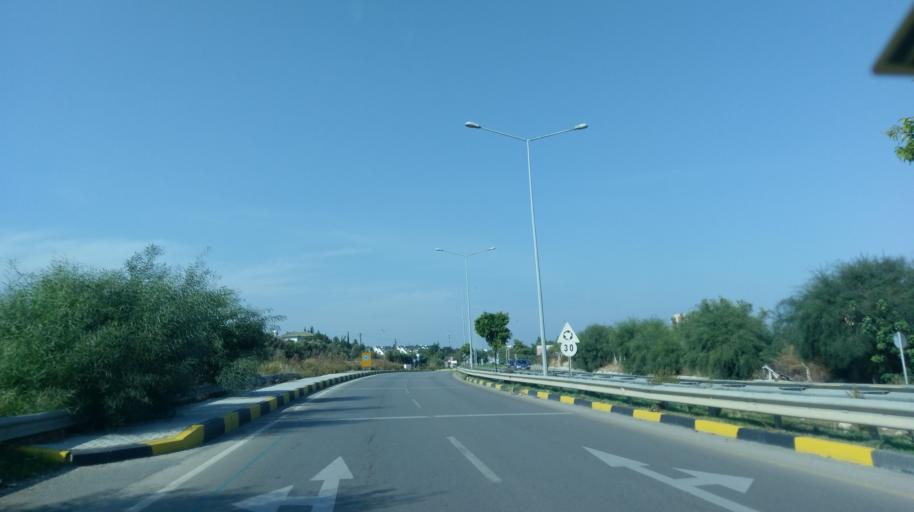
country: CY
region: Keryneia
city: Kyrenia
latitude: 35.3343
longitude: 33.2644
